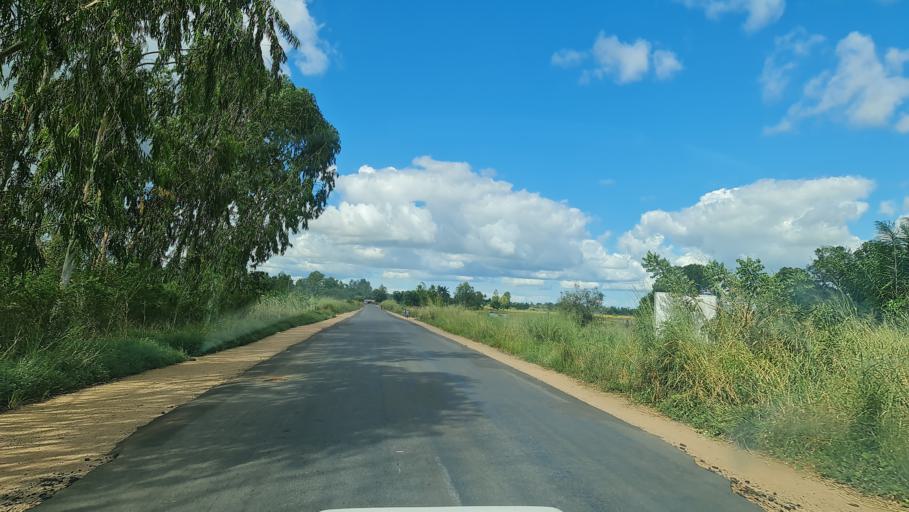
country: MZ
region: Zambezia
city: Quelimane
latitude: -17.6000
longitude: 36.7983
